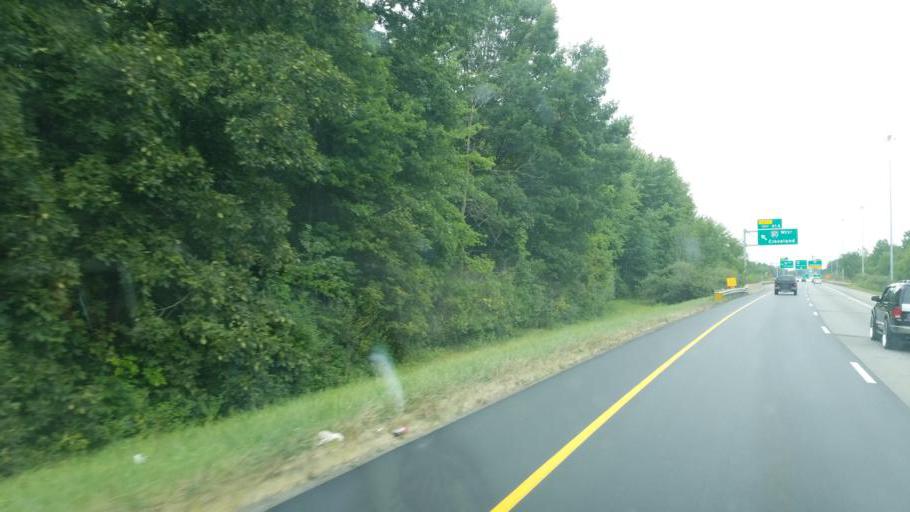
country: US
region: Ohio
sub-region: Mahoning County
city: Austintown
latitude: 41.1189
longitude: -80.7534
